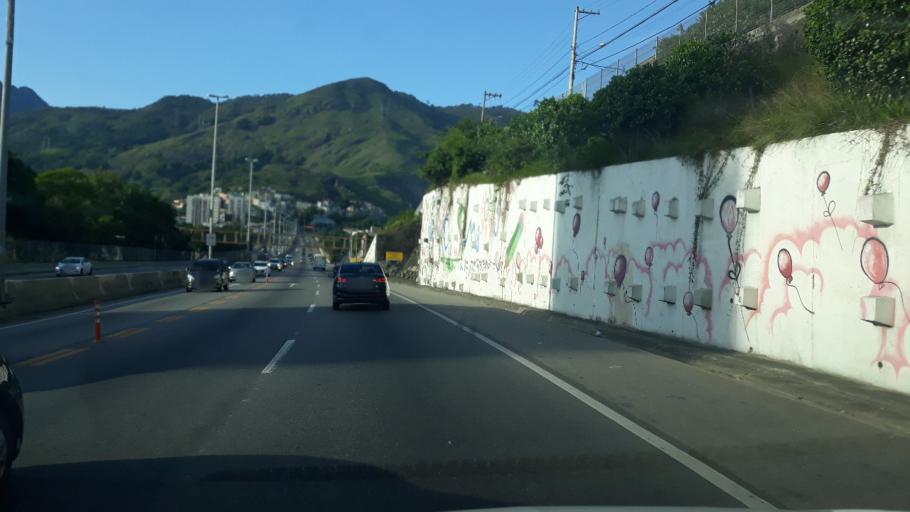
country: BR
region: Rio de Janeiro
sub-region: Rio De Janeiro
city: Rio de Janeiro
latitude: -22.8988
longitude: -43.3028
